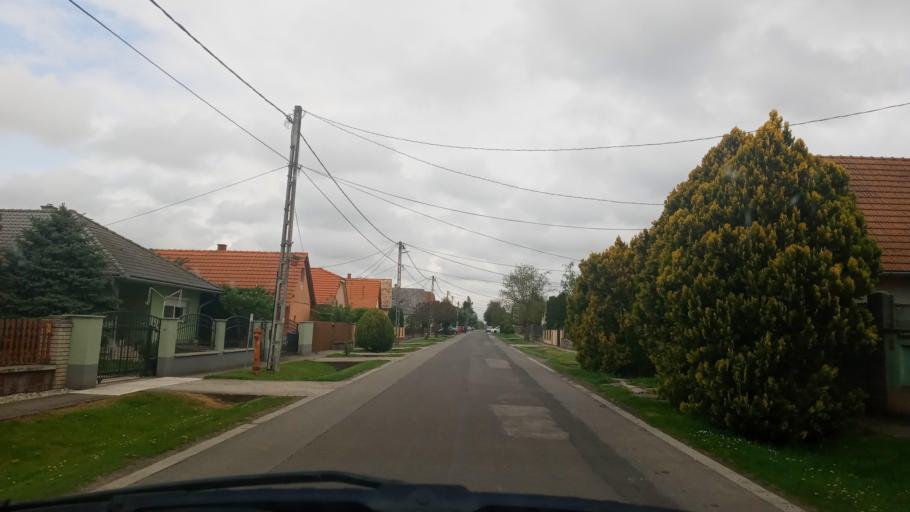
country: HU
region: Baranya
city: Kozarmisleny
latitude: 46.0004
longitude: 18.3753
